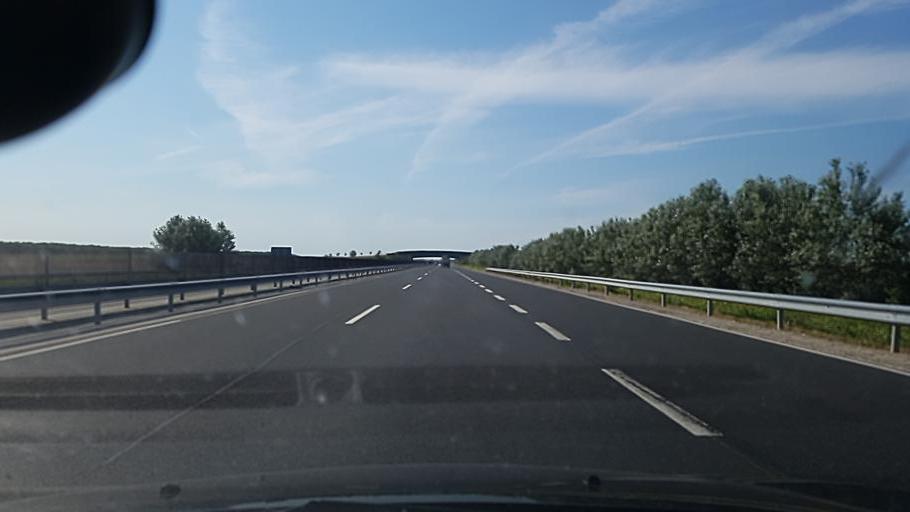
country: HU
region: Tolna
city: Szedres
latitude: 46.4364
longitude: 18.7120
